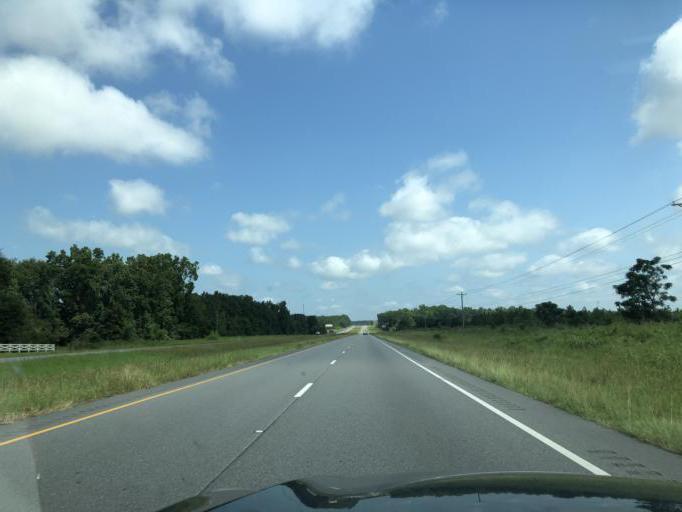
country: US
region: Alabama
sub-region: Houston County
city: Rehobeth
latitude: 31.0500
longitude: -85.4056
